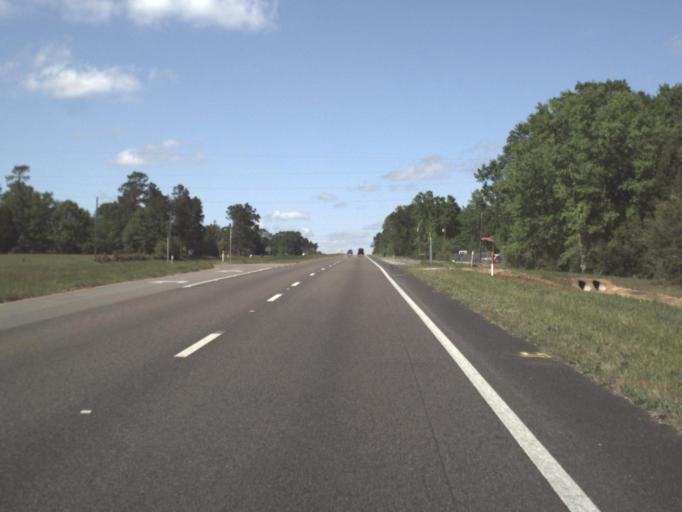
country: US
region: Florida
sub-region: Escambia County
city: Cantonment
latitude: 30.6603
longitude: -87.3514
